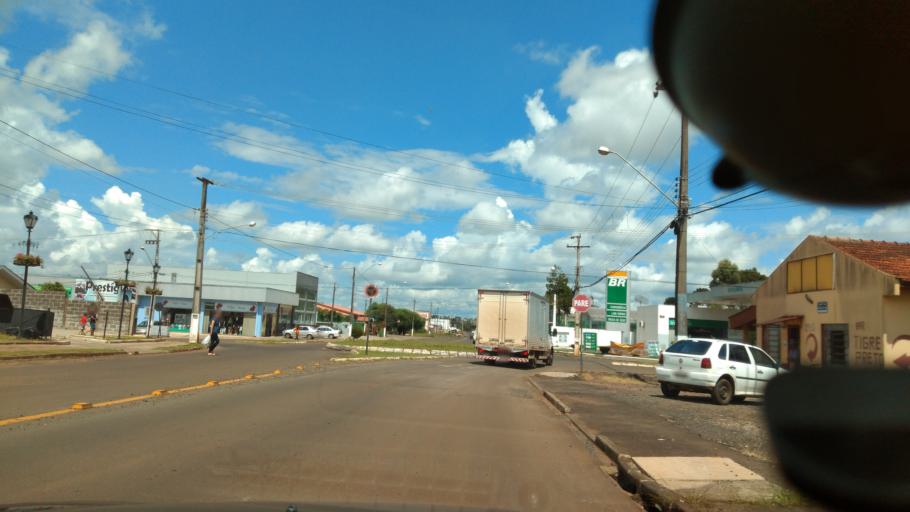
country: BR
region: Parana
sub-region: Guarapuava
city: Guarapuava
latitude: -25.3934
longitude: -51.4921
